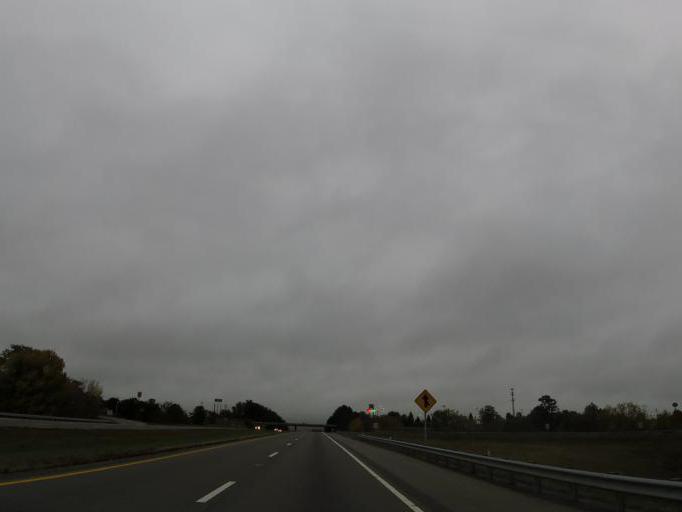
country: US
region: Virginia
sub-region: Wythe County
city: Wytheville
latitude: 36.9707
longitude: -81.0673
